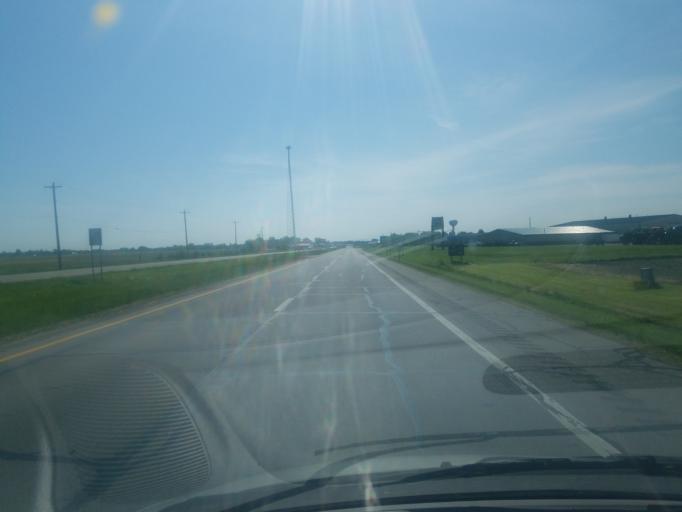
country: US
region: Ohio
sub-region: Huron County
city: Monroeville
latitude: 41.2512
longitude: -82.7158
